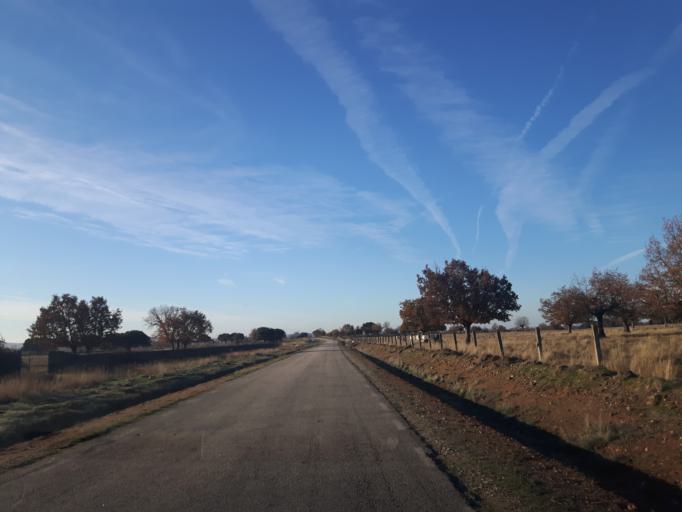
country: ES
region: Castille and Leon
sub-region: Provincia de Salamanca
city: Cerralbo
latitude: 40.9628
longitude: -6.5939
